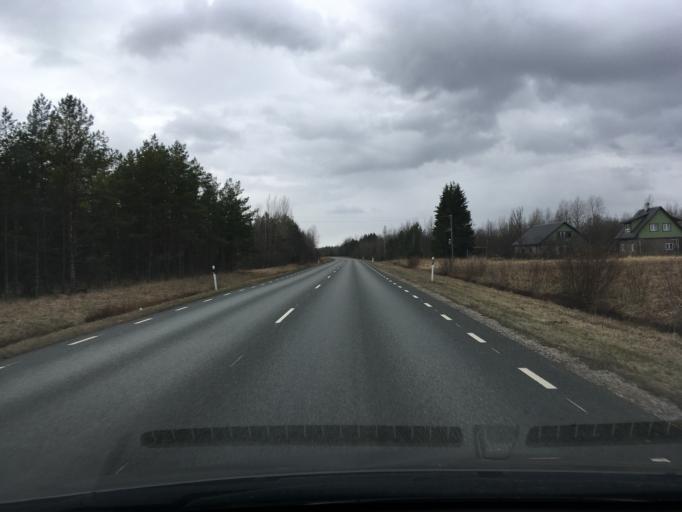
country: EE
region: Laeaene
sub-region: Lihula vald
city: Lihula
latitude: 58.6201
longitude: 23.9055
